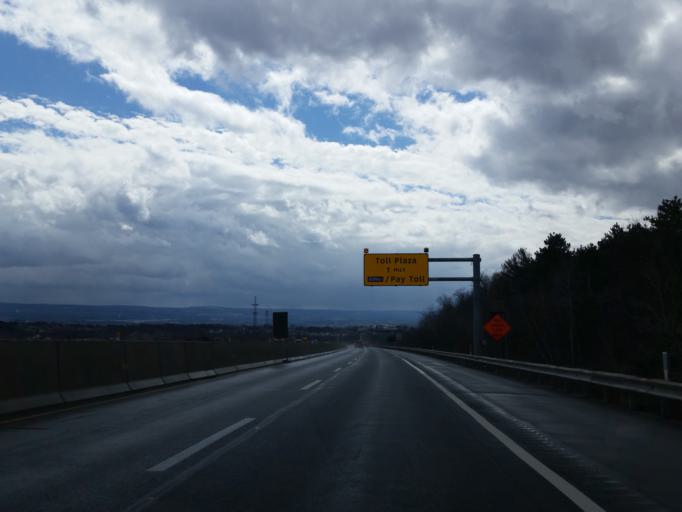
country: US
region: Pennsylvania
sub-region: Lackawanna County
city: Taylor
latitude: 41.3981
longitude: -75.7305
